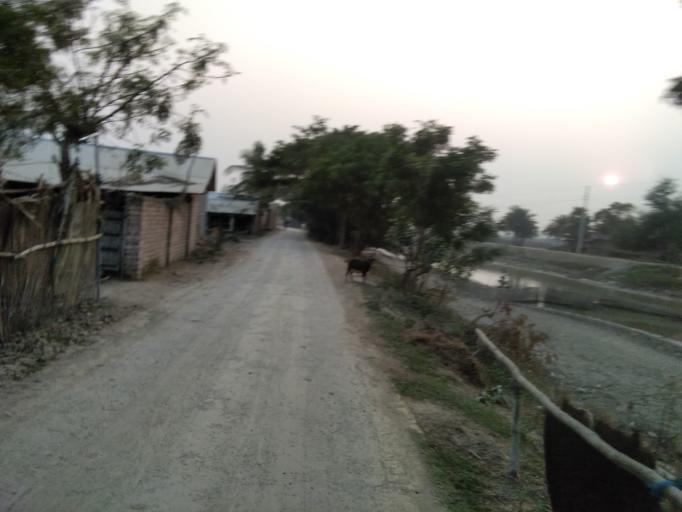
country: BD
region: Khulna
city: Satkhira
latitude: 22.6508
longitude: 89.0147
